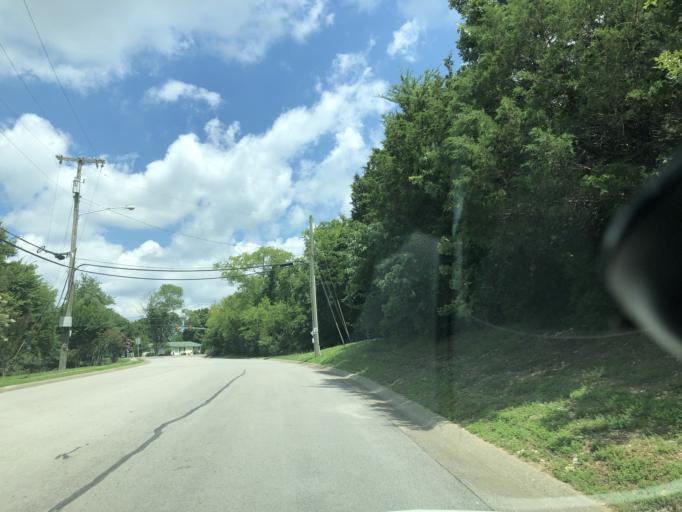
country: US
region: Tennessee
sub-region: Rutherford County
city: La Vergne
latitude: 36.0444
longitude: -86.6272
